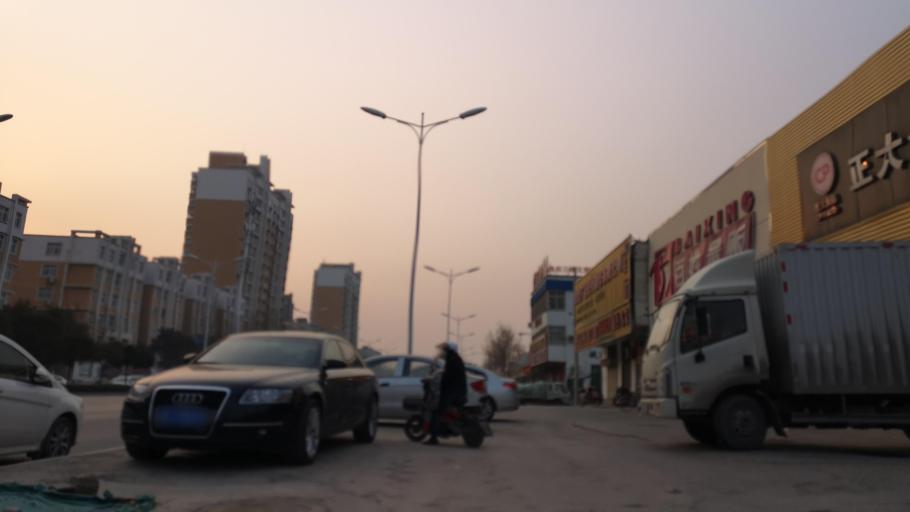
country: CN
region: Henan Sheng
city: Zhongyuanlu
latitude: 35.7893
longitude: 115.0875
